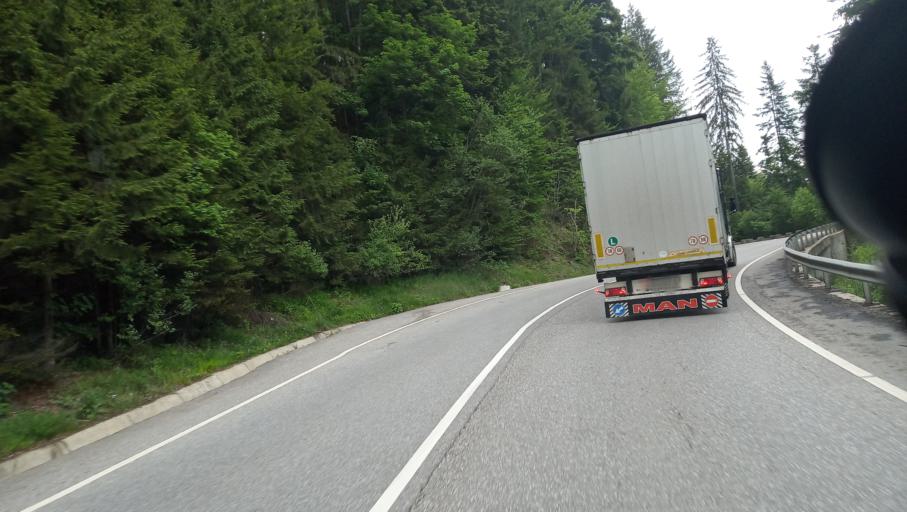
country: RO
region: Neamt
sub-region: Comuna Pipirig
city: Dolhesti
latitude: 47.1660
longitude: 26.0075
